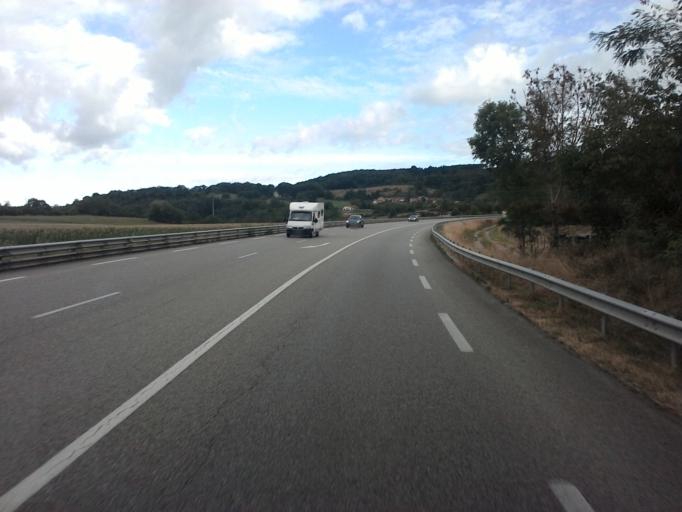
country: FR
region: Rhone-Alpes
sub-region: Departement de l'Ain
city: Lagnieu
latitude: 45.8876
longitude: 5.3397
